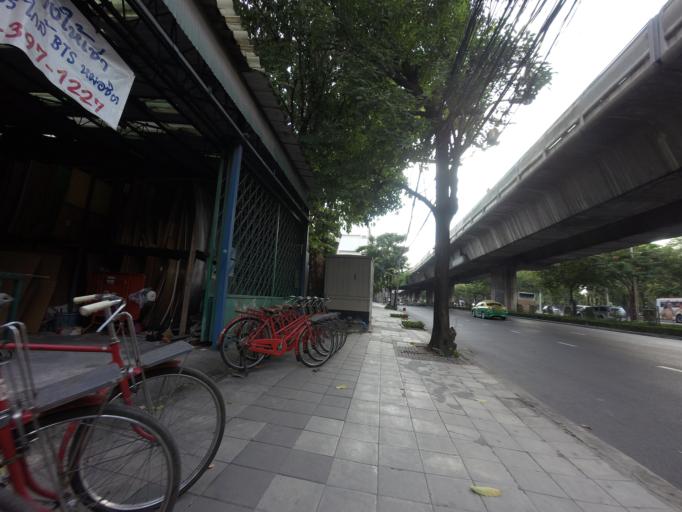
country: TH
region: Bangkok
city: Bang Sue
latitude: 13.8066
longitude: 100.5562
